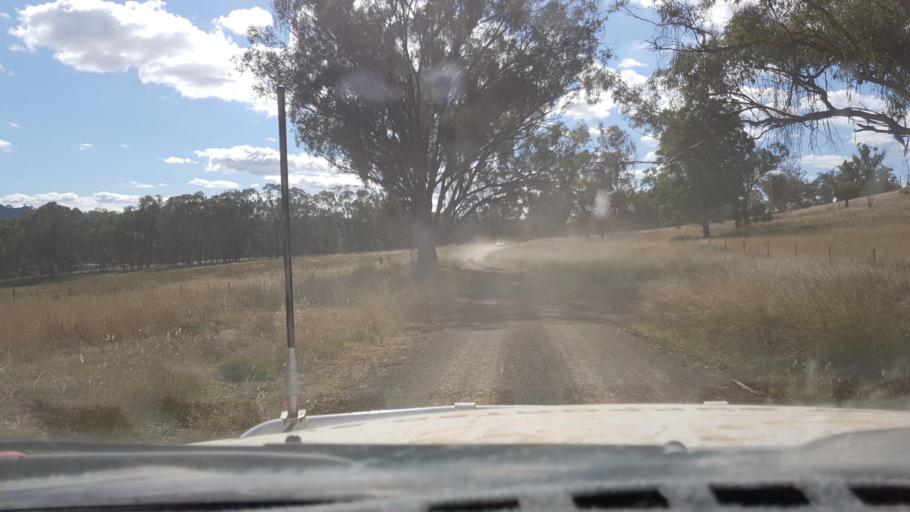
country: AU
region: New South Wales
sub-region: Tamworth Municipality
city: Manilla
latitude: -30.4646
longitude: 150.7786
